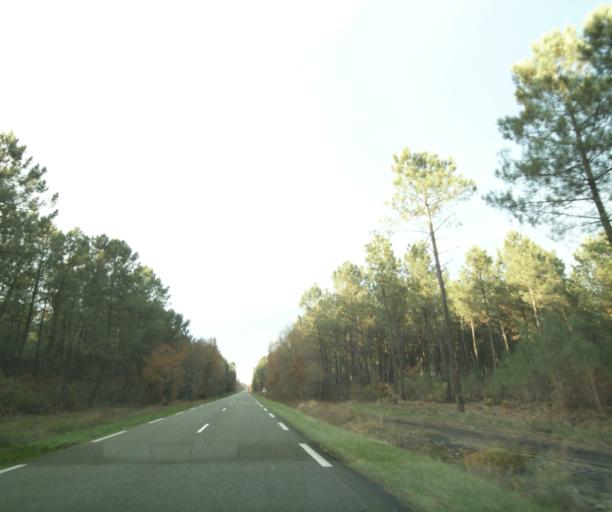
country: FR
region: Aquitaine
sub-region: Departement des Landes
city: Gabarret
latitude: 44.0424
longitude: -0.0368
